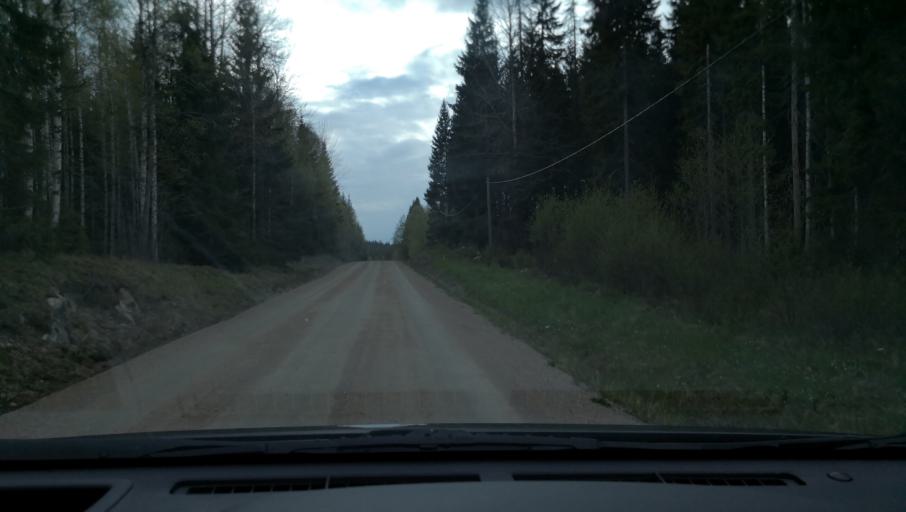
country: SE
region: Vaestmanland
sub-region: Fagersta Kommun
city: Fagersta
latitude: 60.1214
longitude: 15.7284
